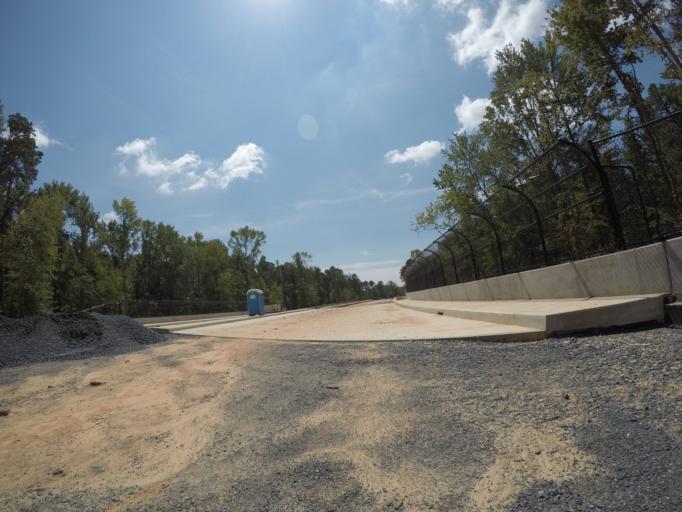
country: US
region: Maryland
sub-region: Anne Arundel County
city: Odenton
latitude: 39.0968
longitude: -76.7060
